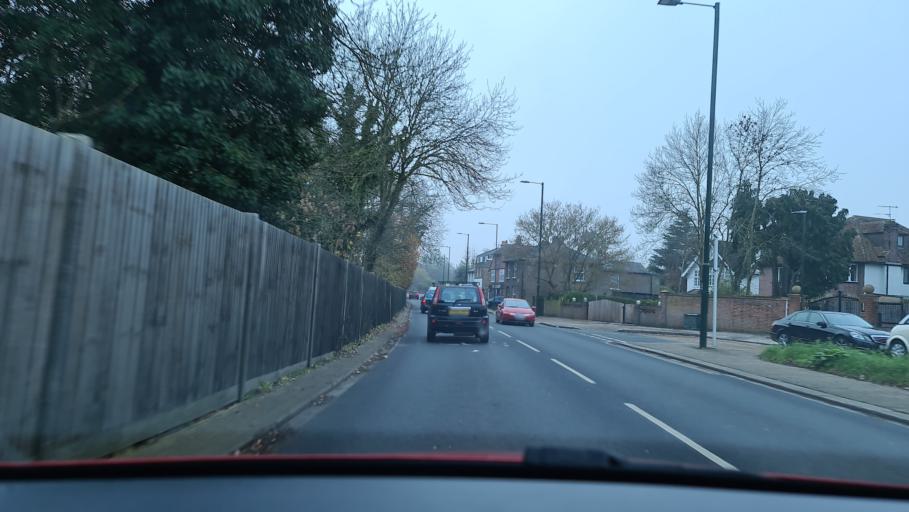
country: GB
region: England
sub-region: Greater London
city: Richmond
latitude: 51.4386
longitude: -0.3044
